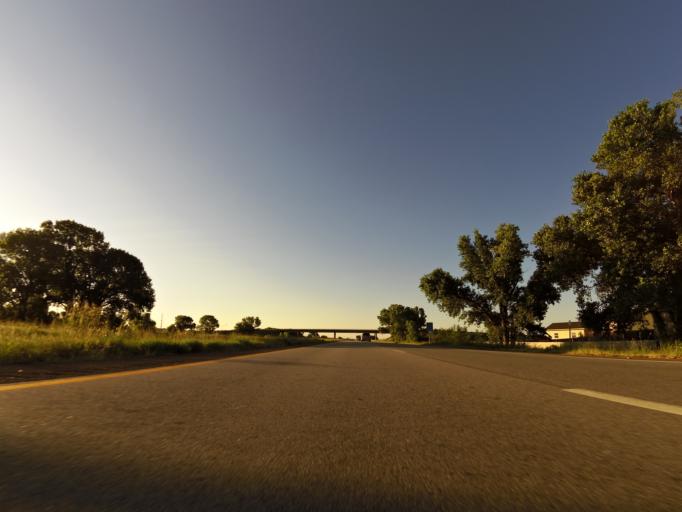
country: US
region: Kansas
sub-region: Sedgwick County
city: Maize
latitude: 37.7681
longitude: -97.4512
